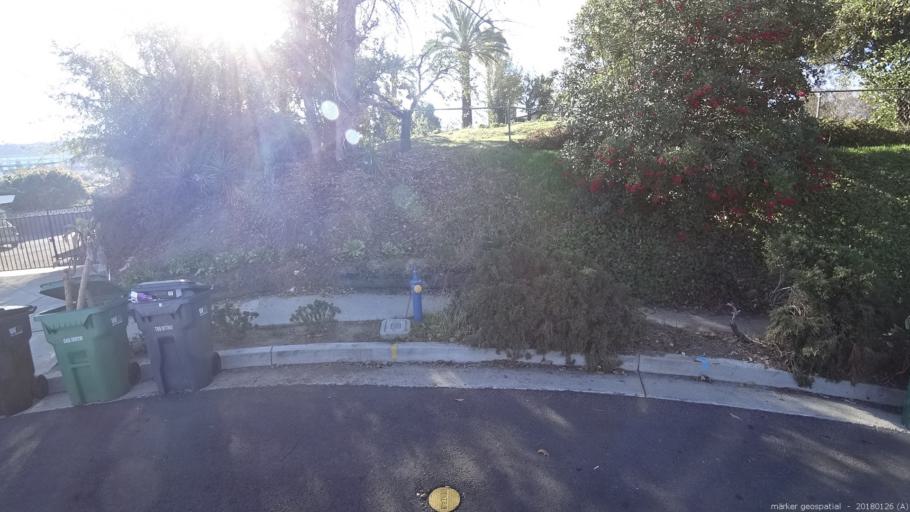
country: US
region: California
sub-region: Los Angeles County
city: Walnut
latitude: 33.9983
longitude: -117.8417
